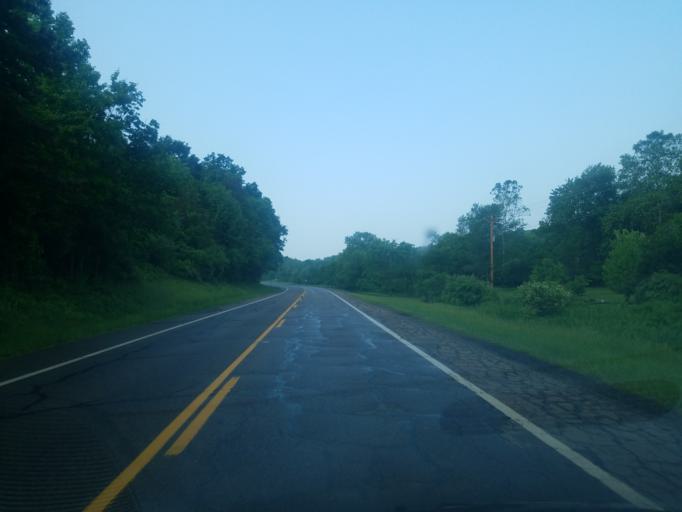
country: US
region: Ohio
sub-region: Tuscarawas County
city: Rockford
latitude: 40.5252
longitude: -81.2549
